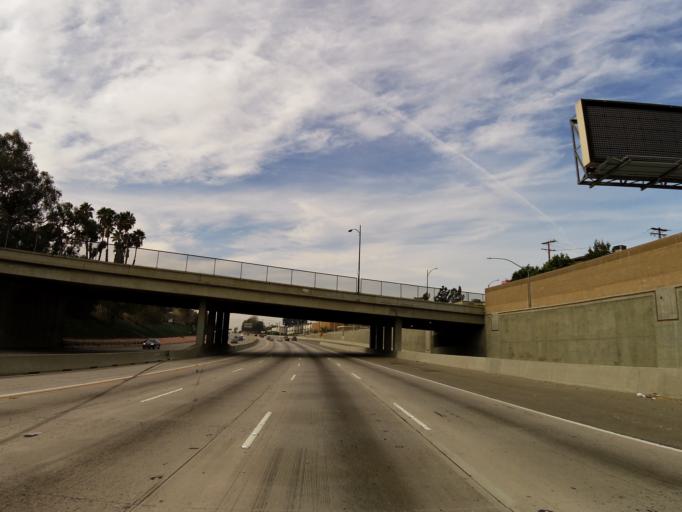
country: US
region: California
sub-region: Los Angeles County
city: Universal City
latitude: 34.1542
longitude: -118.3442
